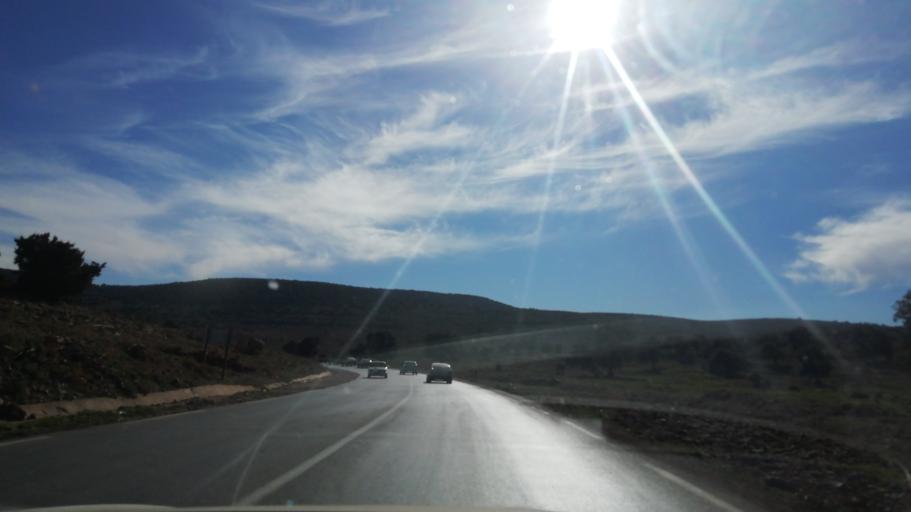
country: DZ
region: Tlemcen
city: Sebdou
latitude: 34.7220
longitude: -1.3390
